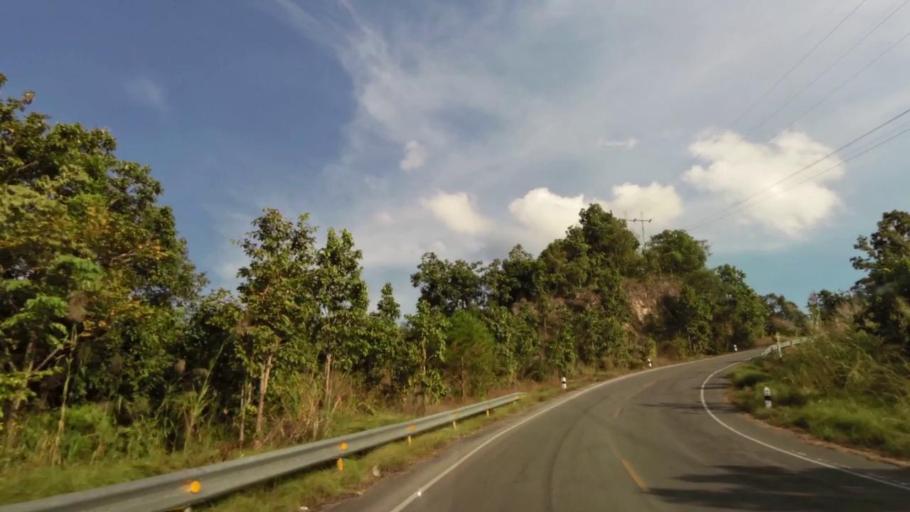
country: TH
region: Chiang Rai
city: Khun Tan
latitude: 19.8783
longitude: 100.3121
